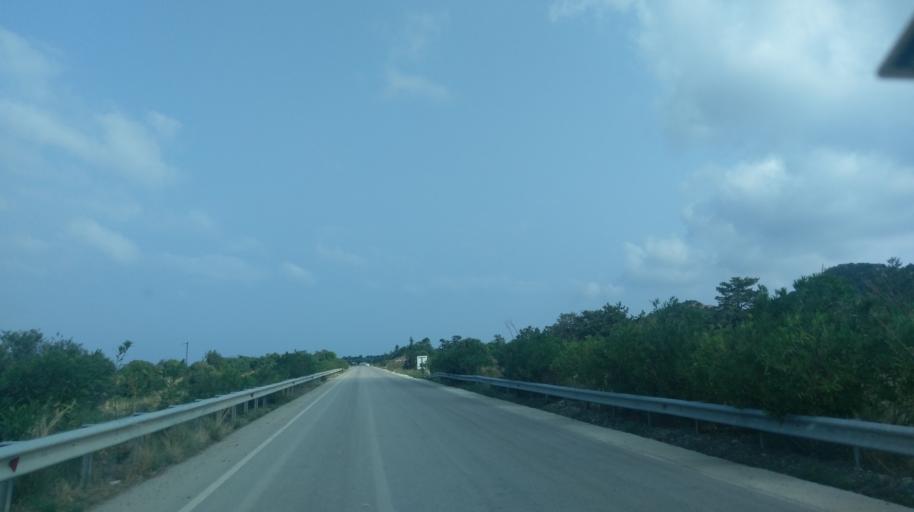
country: CY
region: Ammochostos
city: Lefkonoiko
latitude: 35.3746
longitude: 33.7141
